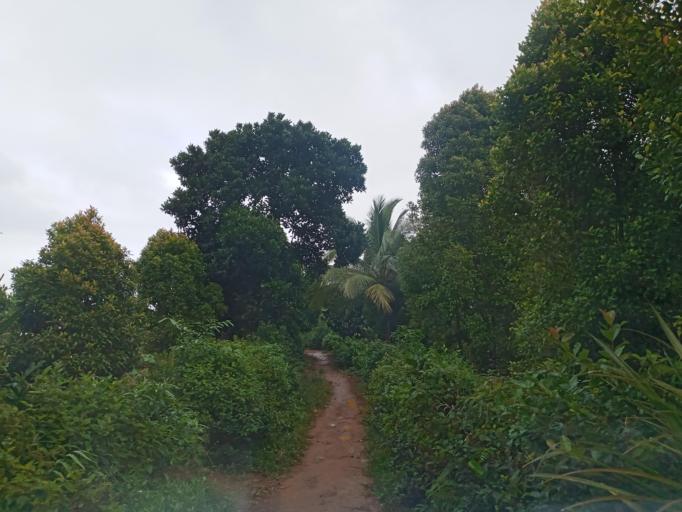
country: MG
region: Atsimo-Atsinanana
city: Vohipaho
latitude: -23.8280
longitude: 47.5433
